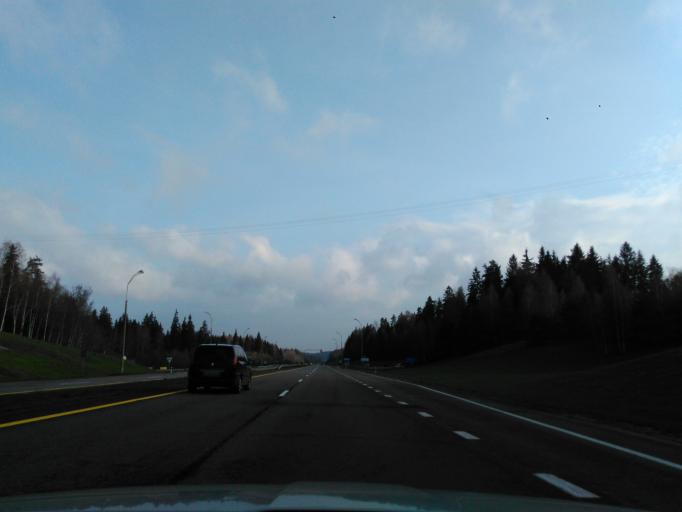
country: BY
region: Minsk
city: Lahoysk
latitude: 54.1349
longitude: 27.8085
